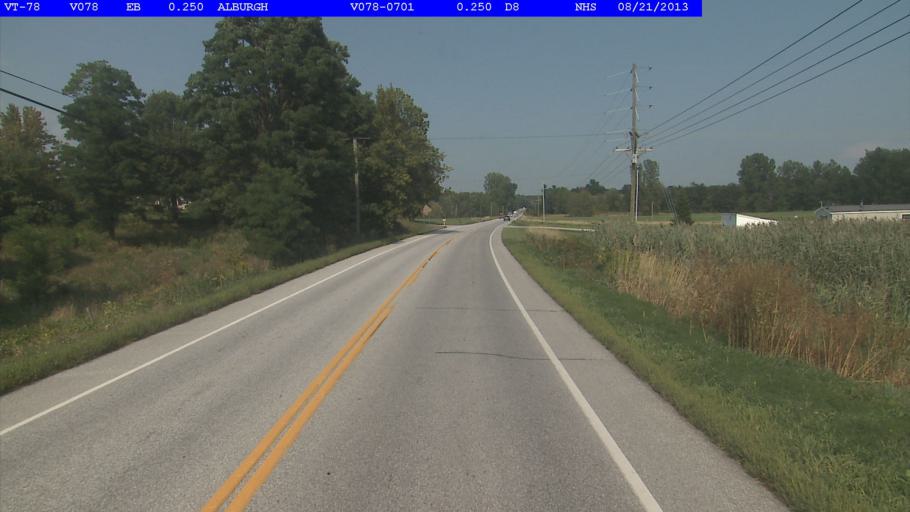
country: US
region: New York
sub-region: Clinton County
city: Rouses Point
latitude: 44.9629
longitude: -73.2744
